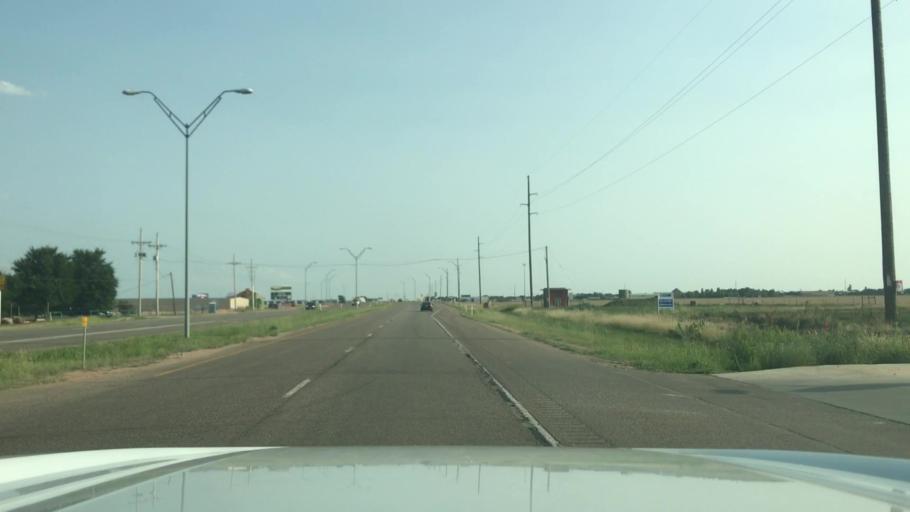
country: US
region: Texas
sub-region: Potter County
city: Bushland
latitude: 35.1260
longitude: -101.9381
